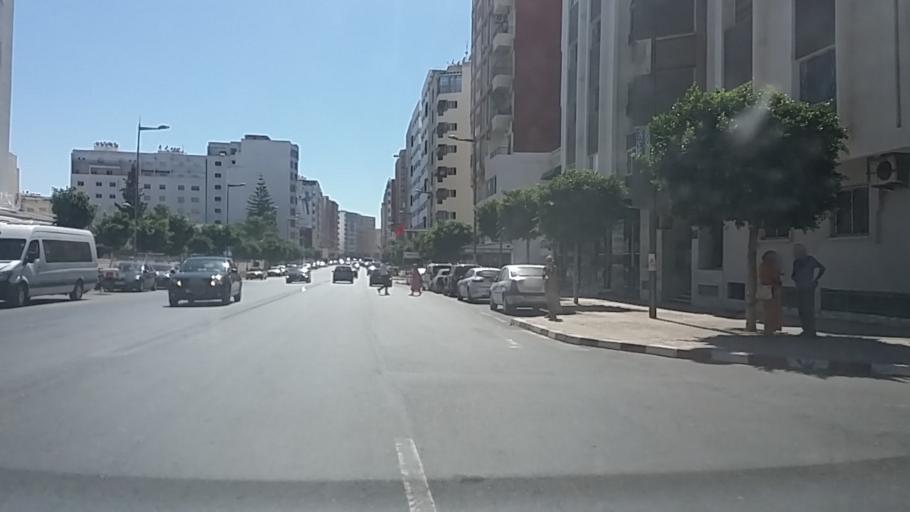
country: MA
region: Gharb-Chrarda-Beni Hssen
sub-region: Kenitra Province
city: Kenitra
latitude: 34.2576
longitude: -6.5898
